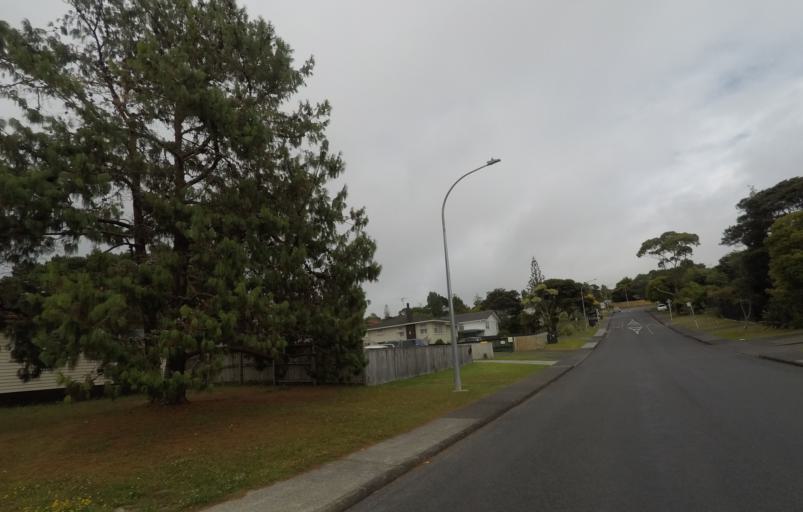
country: NZ
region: Auckland
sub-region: Auckland
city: Titirangi
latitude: -36.9340
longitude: 174.6690
